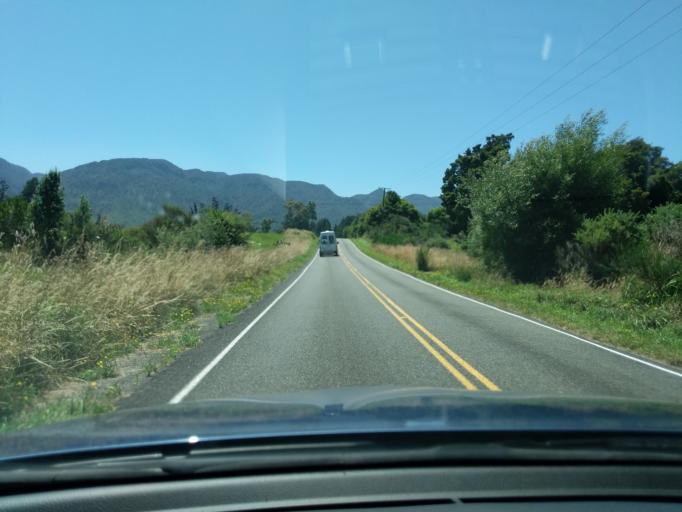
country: NZ
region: Tasman
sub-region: Tasman District
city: Takaka
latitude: -40.7092
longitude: 172.6369
